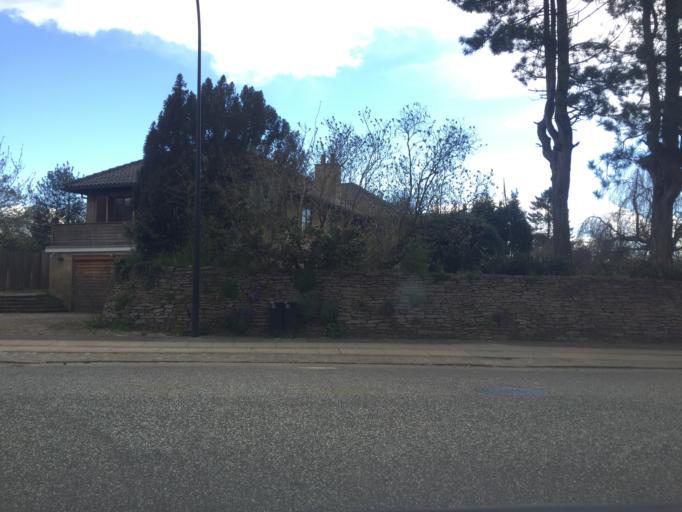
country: DK
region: Capital Region
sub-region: Gentofte Kommune
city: Charlottenlund
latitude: 55.7674
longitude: 12.5664
